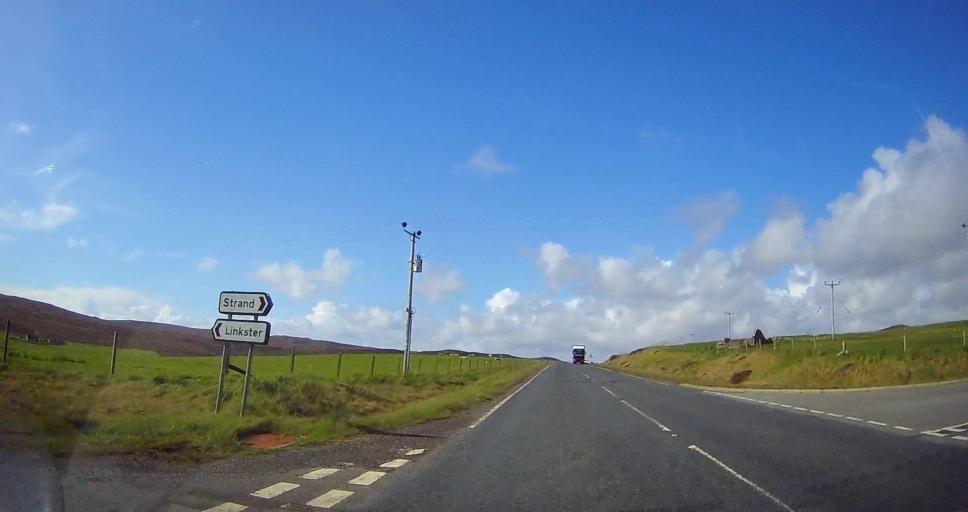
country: GB
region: Scotland
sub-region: Shetland Islands
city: Lerwick
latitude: 60.1983
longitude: -1.2323
